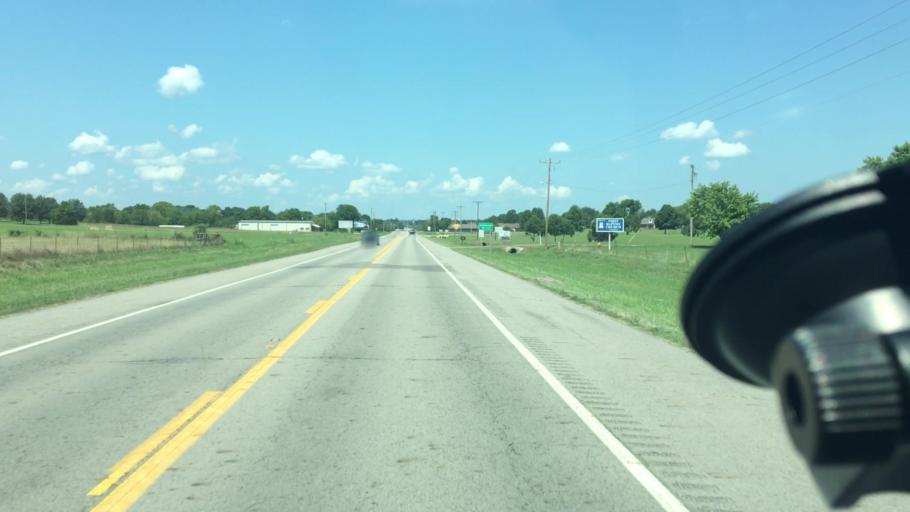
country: US
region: Arkansas
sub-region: Franklin County
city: Charleston
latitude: 35.2966
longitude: -94.0101
